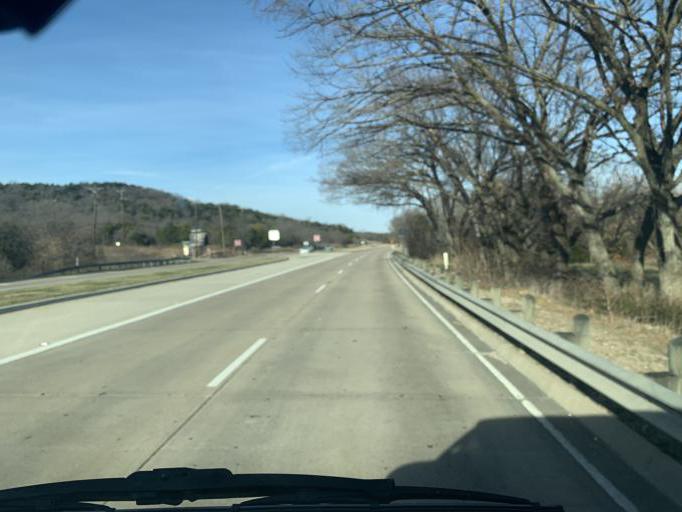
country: US
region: Texas
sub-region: Dallas County
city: Cedar Hill
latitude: 32.6141
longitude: -96.9687
